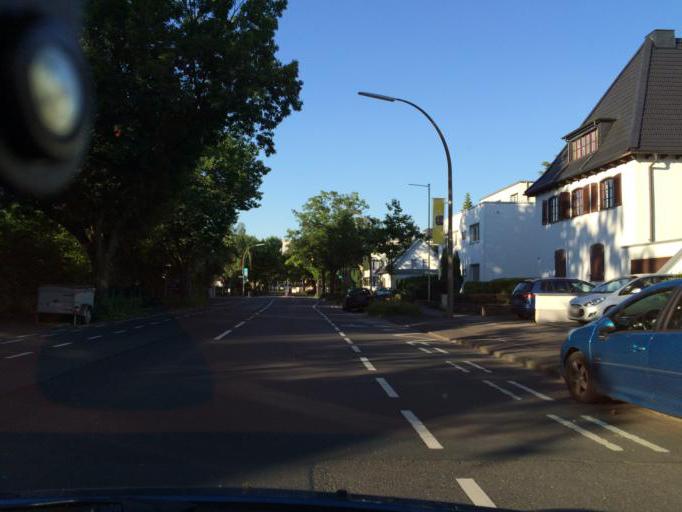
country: DE
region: North Rhine-Westphalia
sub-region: Regierungsbezirk Koln
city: Konigswinter
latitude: 50.6986
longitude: 7.1454
